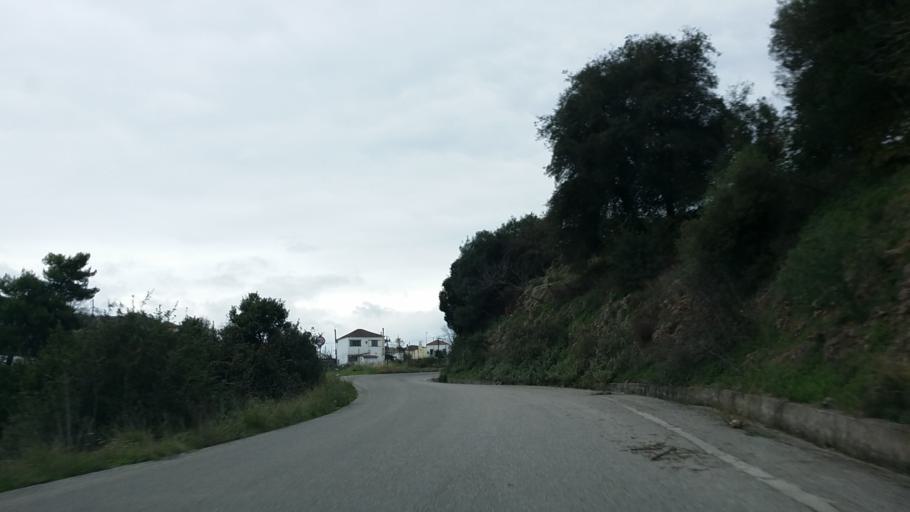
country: GR
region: West Greece
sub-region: Nomos Aitolias kai Akarnanias
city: Fitiai
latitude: 38.7116
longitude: 21.1701
